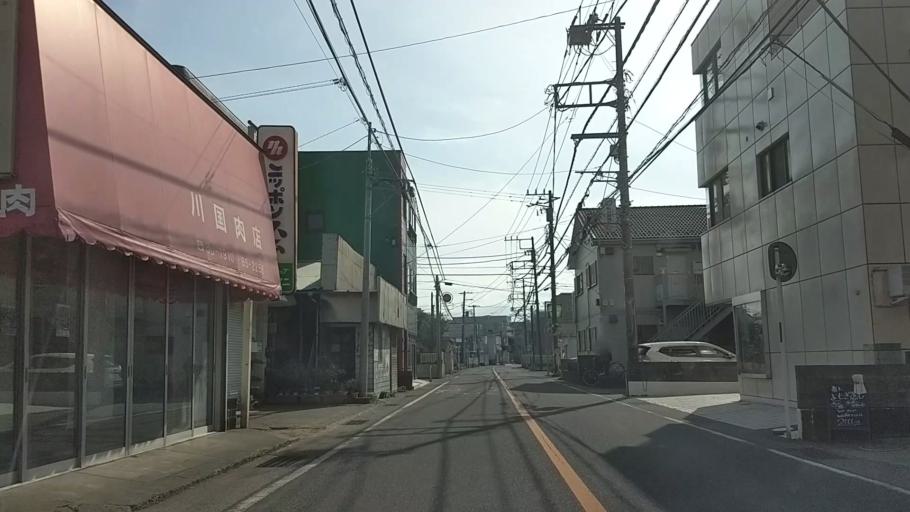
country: JP
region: Kanagawa
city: Chigasaki
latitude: 35.3371
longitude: 139.3829
